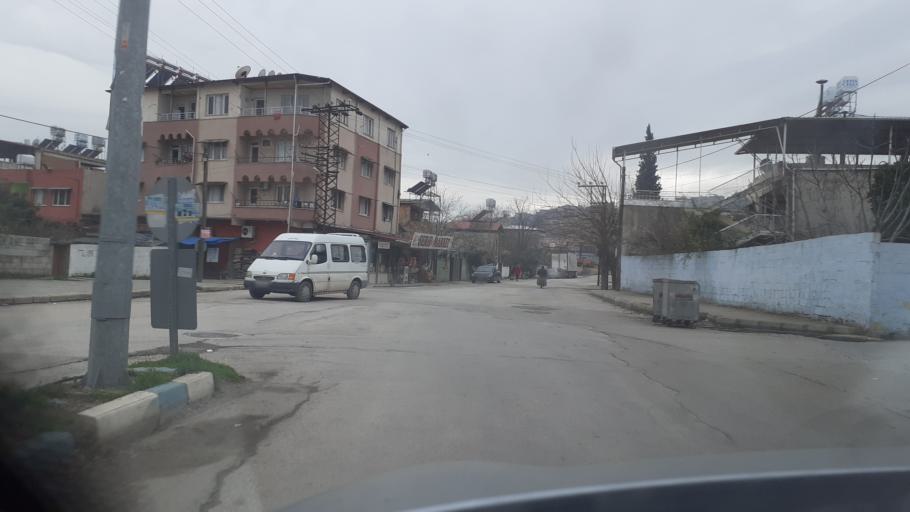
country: TR
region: Hatay
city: Kirikhan
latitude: 36.4910
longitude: 36.3562
